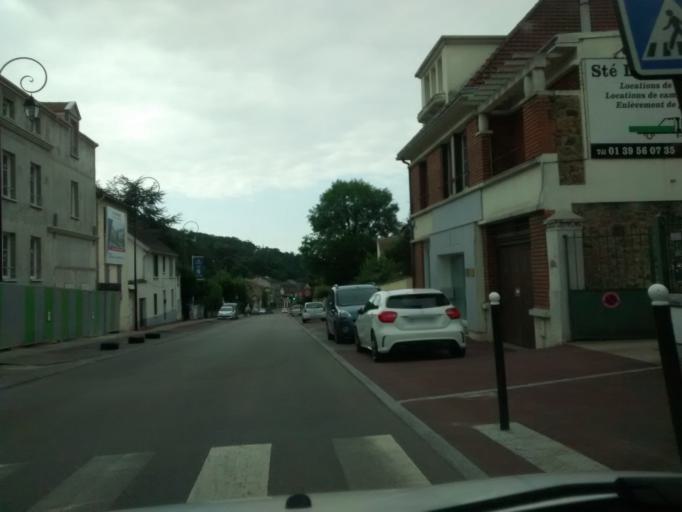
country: FR
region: Ile-de-France
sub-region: Departement des Yvelines
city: Buc
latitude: 48.7838
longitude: 2.1324
